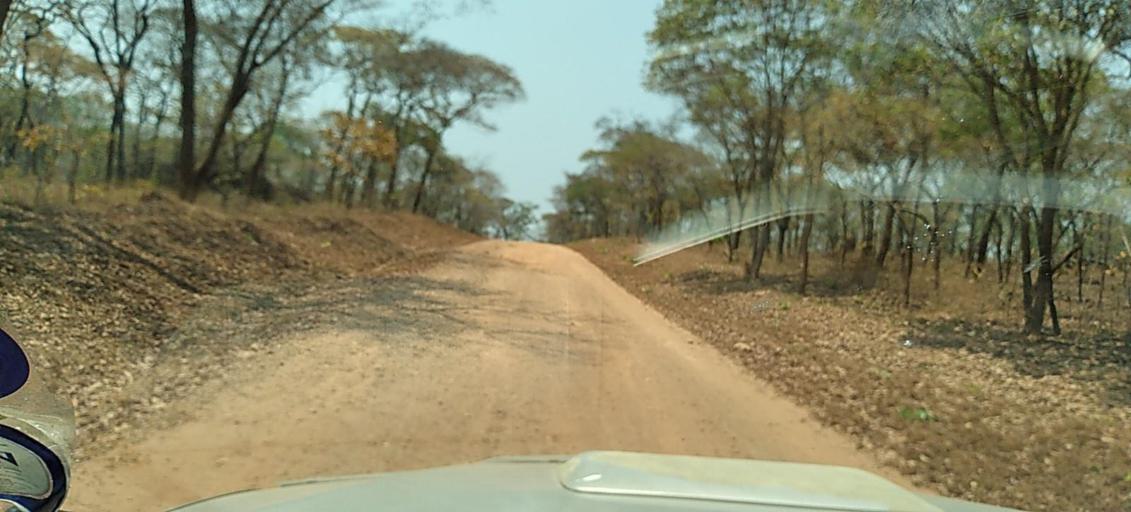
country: ZM
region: North-Western
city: Kasempa
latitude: -13.5488
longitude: 26.0606
